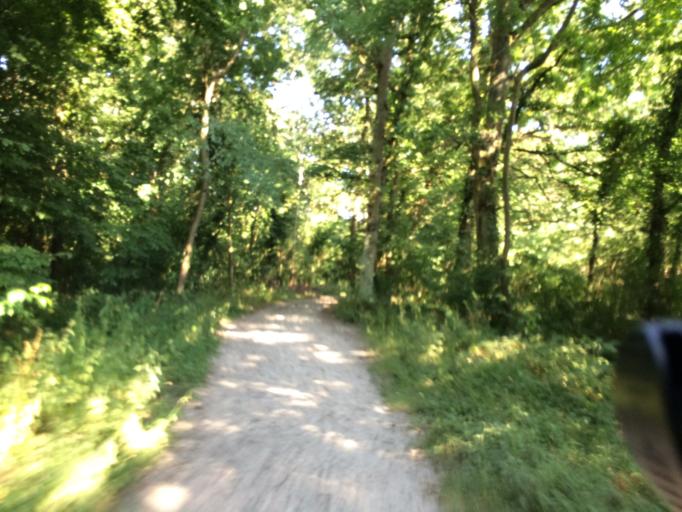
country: FR
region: Ile-de-France
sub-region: Departement de l'Essonne
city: Soisy-sur-Seine
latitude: 48.6513
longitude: 2.4696
